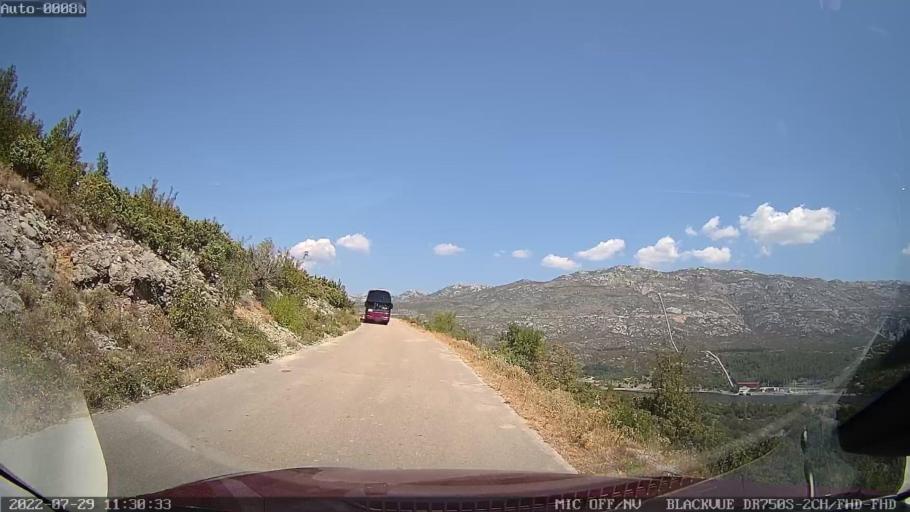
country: HR
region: Zadarska
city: Obrovac
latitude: 44.1981
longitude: 15.7496
